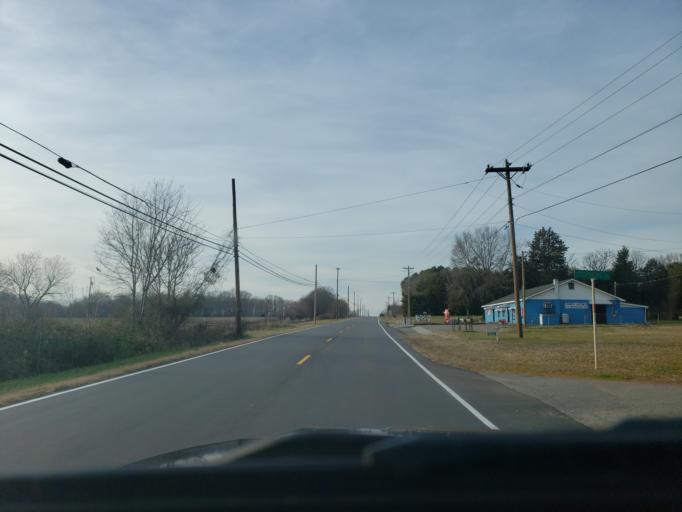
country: US
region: North Carolina
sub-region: Cleveland County
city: Boiling Springs
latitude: 35.3073
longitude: -81.7297
